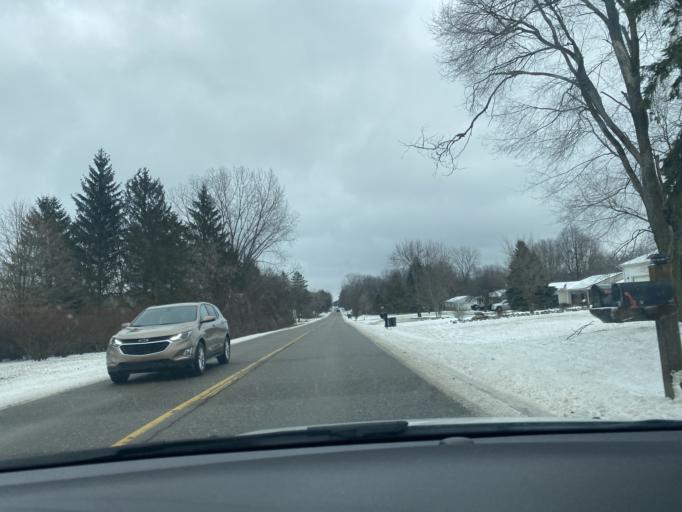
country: US
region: Michigan
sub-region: Lapeer County
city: Barnes Lake-Millers Lake
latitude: 43.2049
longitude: -83.3020
